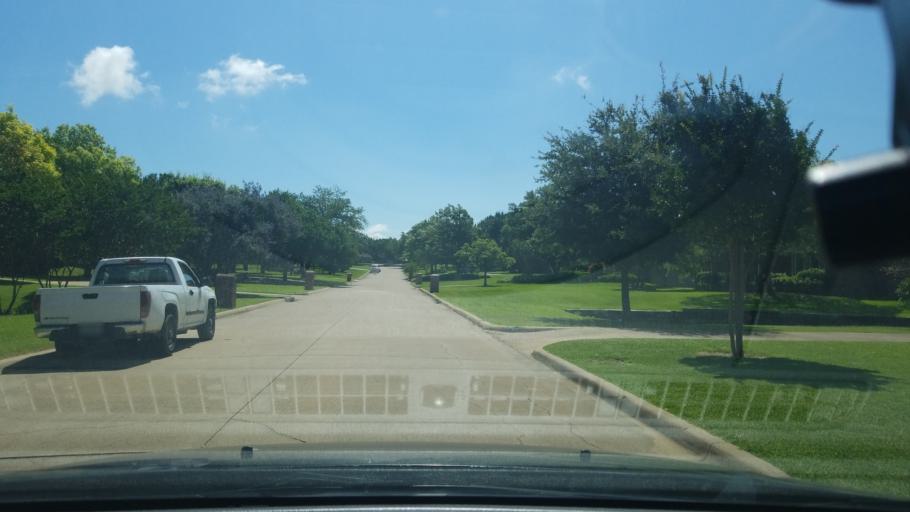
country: US
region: Texas
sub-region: Dallas County
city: Sunnyvale
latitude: 32.7983
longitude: -96.5916
